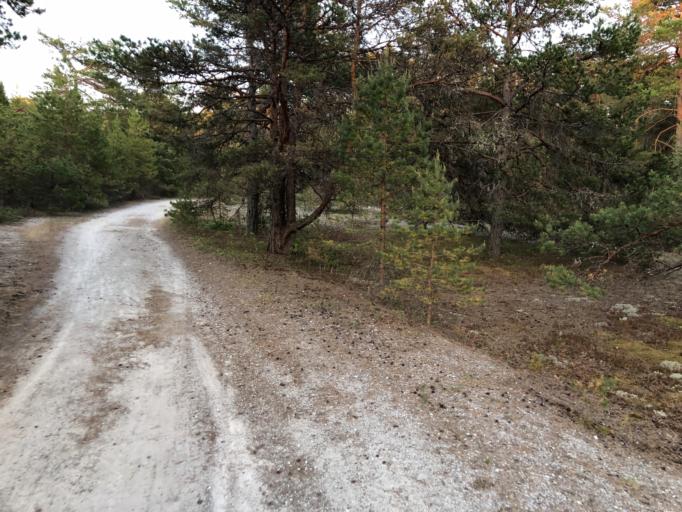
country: EE
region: Harju
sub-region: Paldiski linn
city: Paldiski
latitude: 59.3903
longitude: 24.2313
